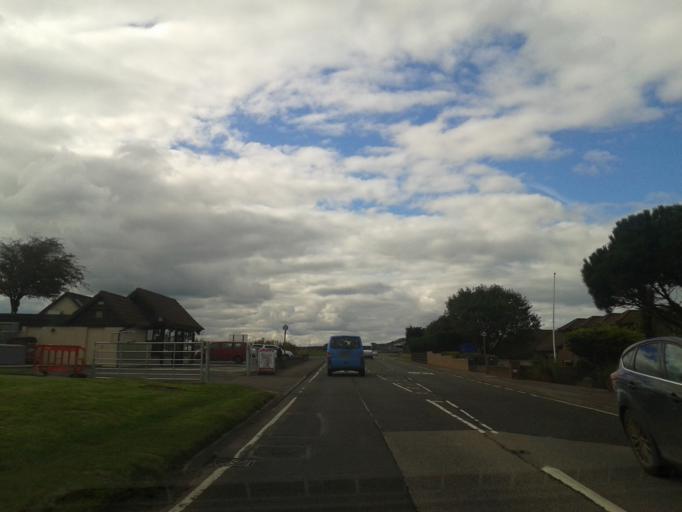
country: GB
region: Scotland
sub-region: Fife
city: Leuchars
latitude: 56.3586
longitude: -2.8770
